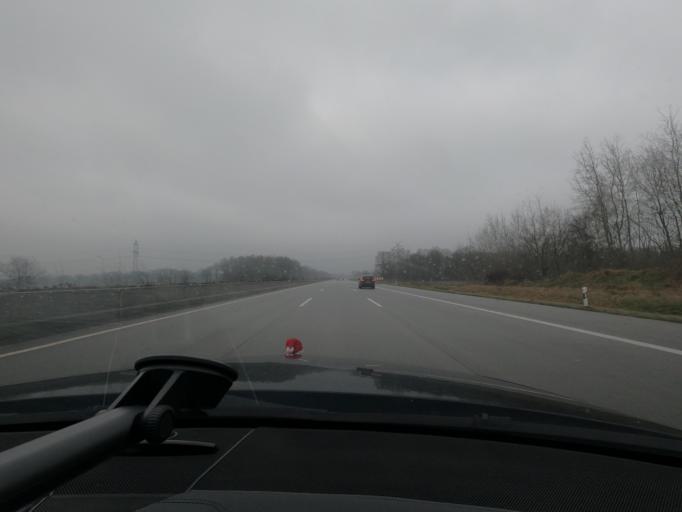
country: DE
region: Schleswig-Holstein
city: Schmalfeld
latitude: 53.8889
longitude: 9.9427
